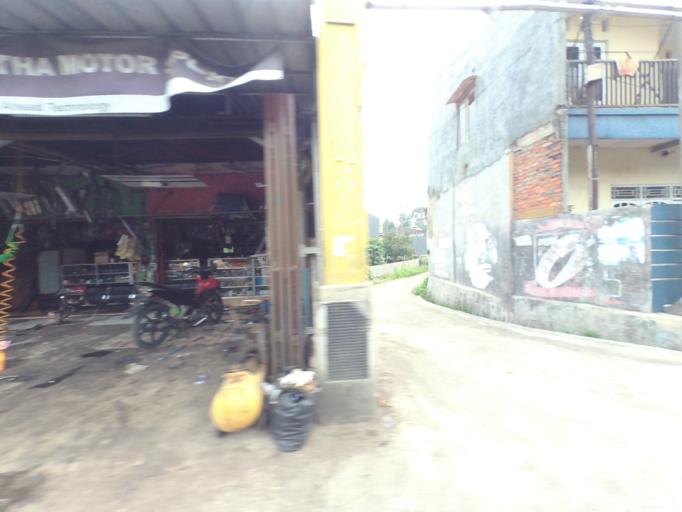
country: ID
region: West Java
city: Ciampea
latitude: -6.5594
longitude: 106.6873
